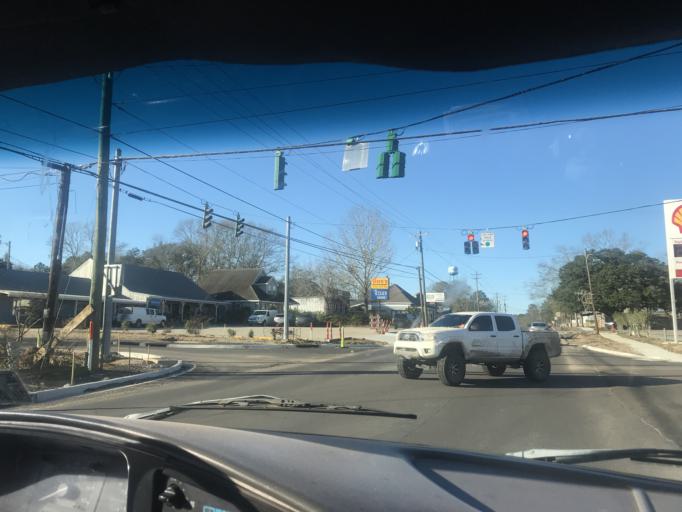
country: US
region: Louisiana
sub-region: Saint Tammany Parish
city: Covington
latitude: 30.6300
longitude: -90.1876
